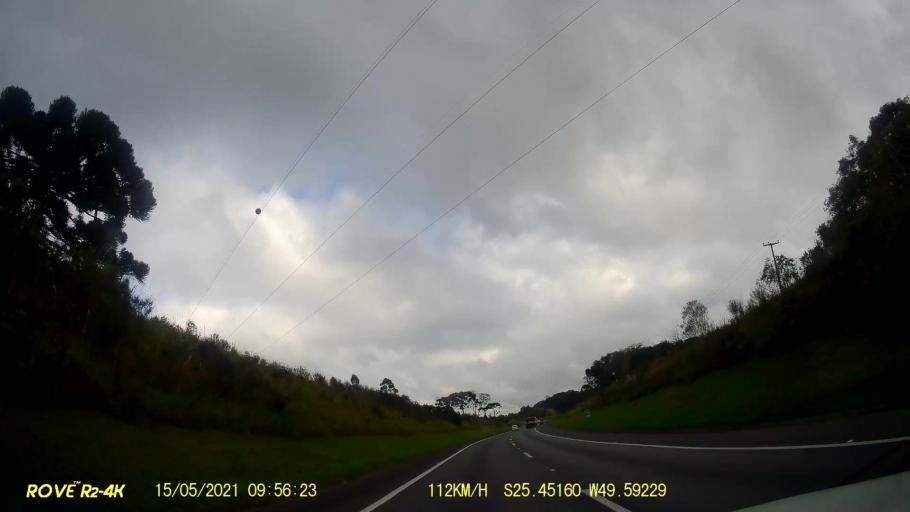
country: BR
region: Parana
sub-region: Campo Largo
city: Campo Largo
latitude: -25.4510
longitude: -49.5925
